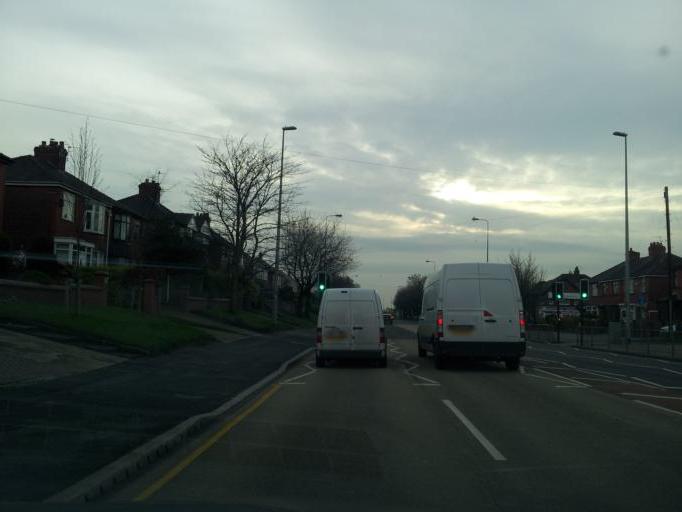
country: GB
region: England
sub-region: Borough of Oldham
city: Oldham
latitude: 53.5373
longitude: -2.1512
